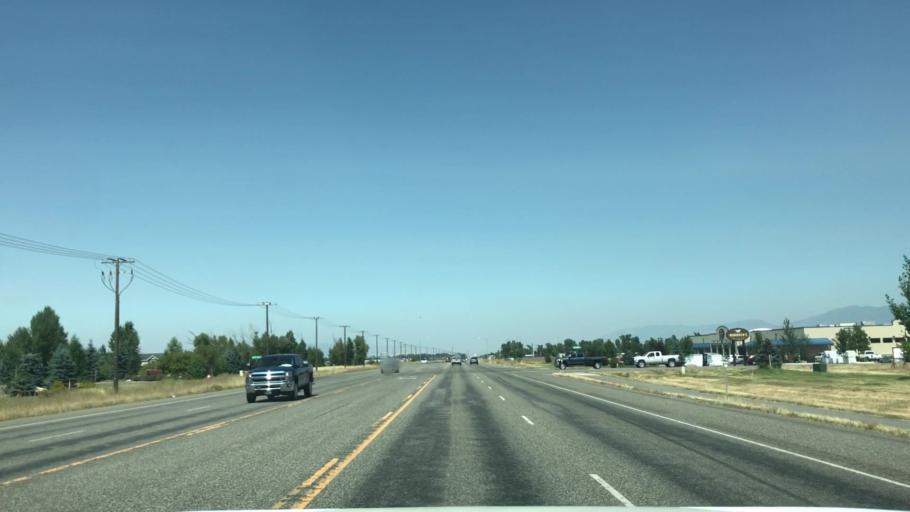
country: US
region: Montana
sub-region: Gallatin County
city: Four Corners
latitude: 45.6814
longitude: -111.1858
